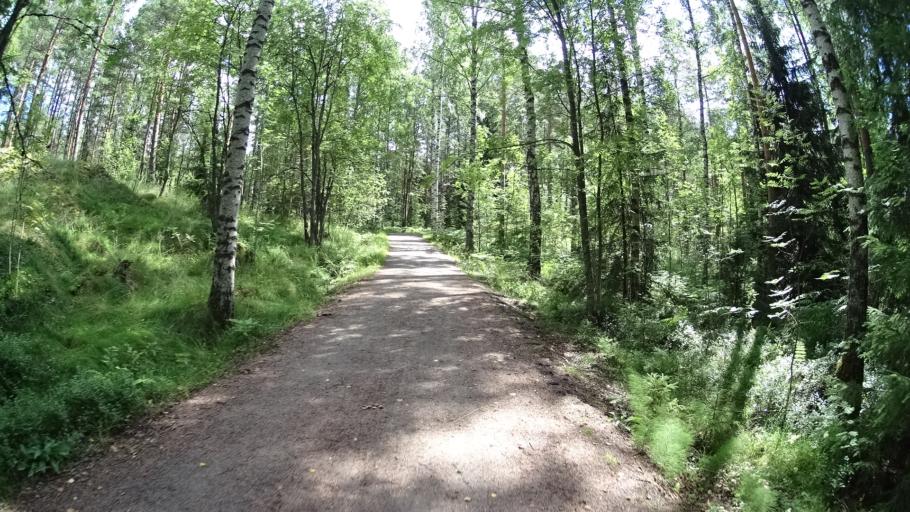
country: FI
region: Uusimaa
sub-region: Helsinki
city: Espoo
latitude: 60.3202
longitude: 24.6771
